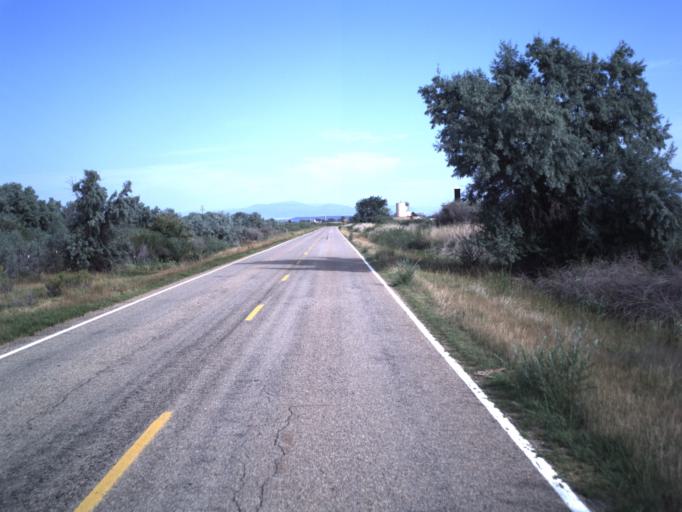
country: US
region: Utah
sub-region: Duchesne County
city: Duchesne
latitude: 40.3307
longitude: -110.2704
